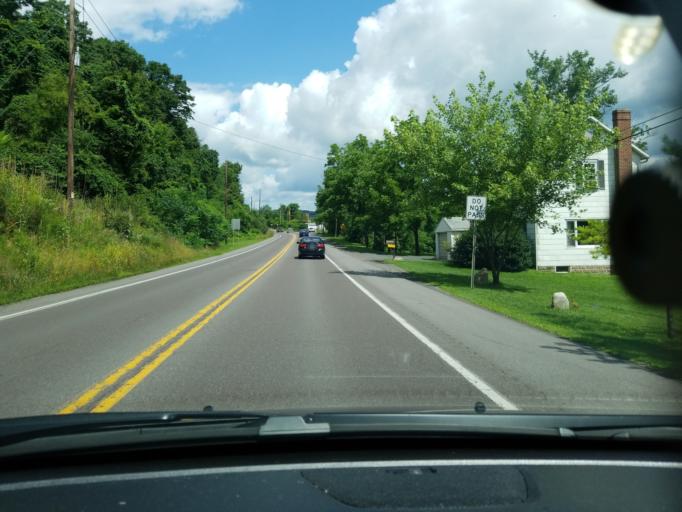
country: US
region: Pennsylvania
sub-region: Northumberland County
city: Kulpmont
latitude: 40.8305
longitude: -76.5044
